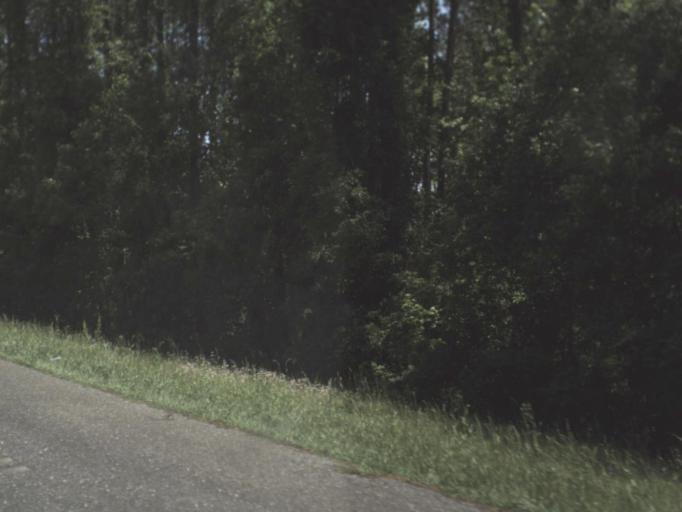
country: US
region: Florida
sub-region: Jefferson County
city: Monticello
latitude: 30.4784
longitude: -83.9258
